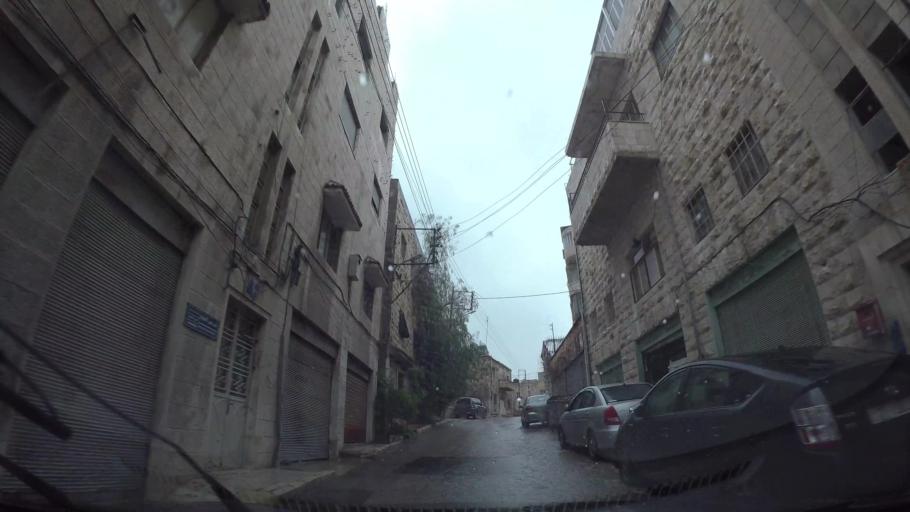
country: JO
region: Amman
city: Amman
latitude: 31.9528
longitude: 35.9284
